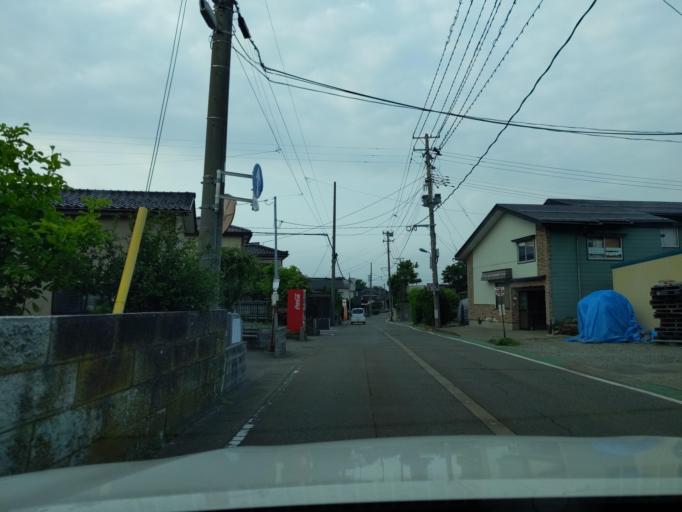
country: JP
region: Niigata
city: Kashiwazaki
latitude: 37.3821
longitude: 138.5731
